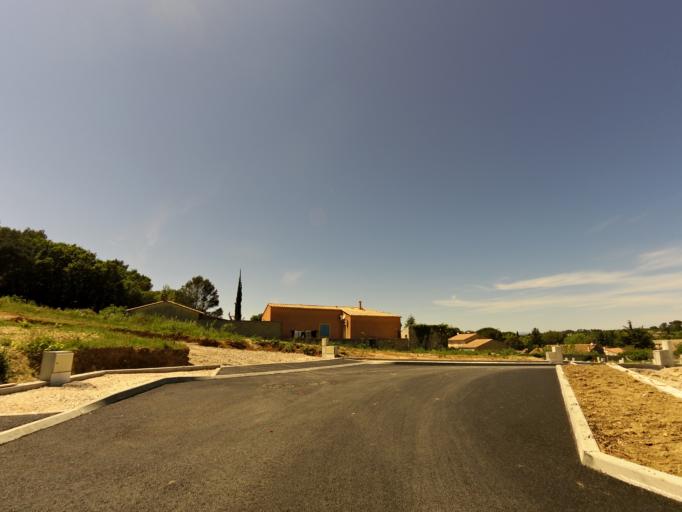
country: FR
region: Languedoc-Roussillon
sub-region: Departement du Gard
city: Aigues-Vives
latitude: 43.7379
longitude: 4.1751
